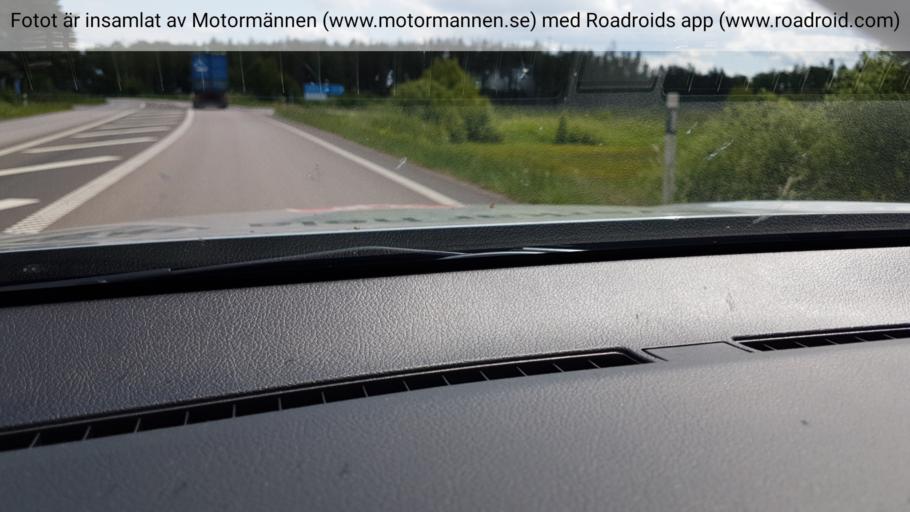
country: SE
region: Vaestra Goetaland
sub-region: Lidkopings Kommun
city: Vinninga
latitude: 58.4318
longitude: 13.2906
